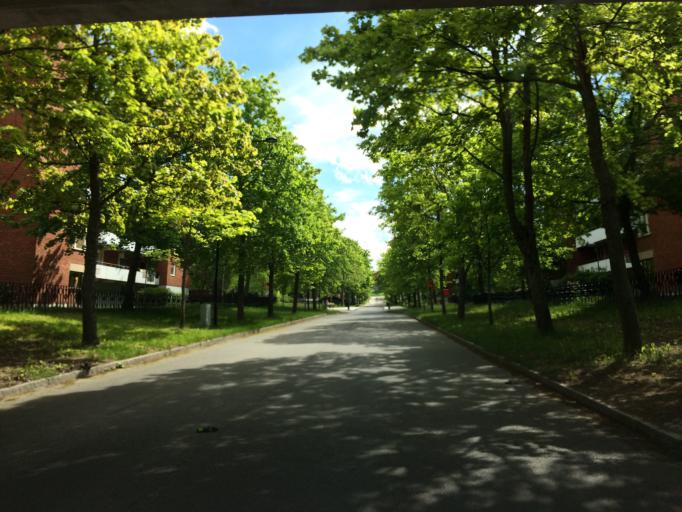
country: SE
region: Stockholm
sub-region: Botkyrka Kommun
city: Fittja
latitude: 59.2670
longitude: 17.8877
